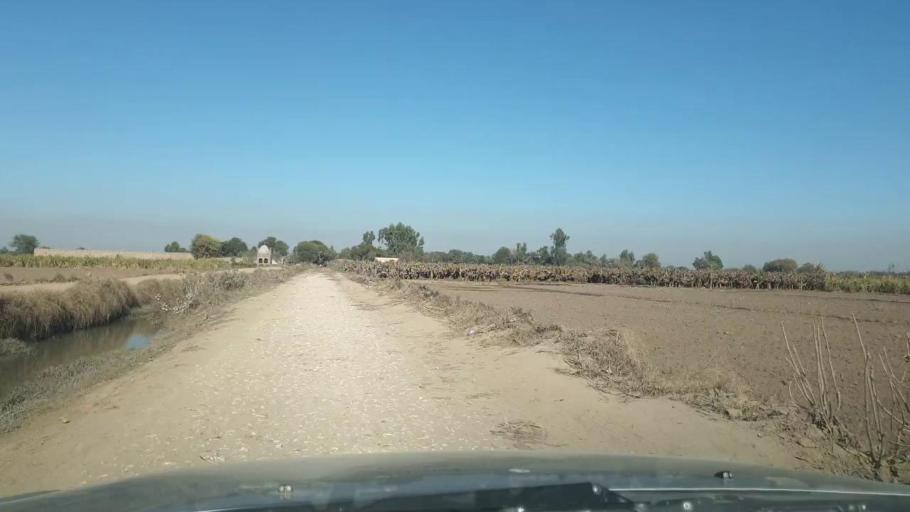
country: PK
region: Sindh
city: Ghotki
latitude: 28.0405
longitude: 69.2467
